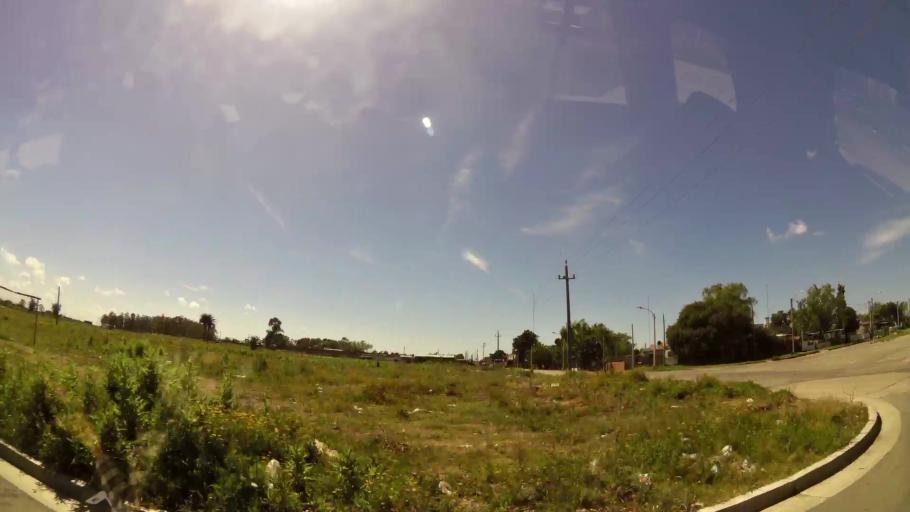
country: UY
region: Canelones
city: Paso de Carrasco
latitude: -34.8510
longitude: -56.1152
